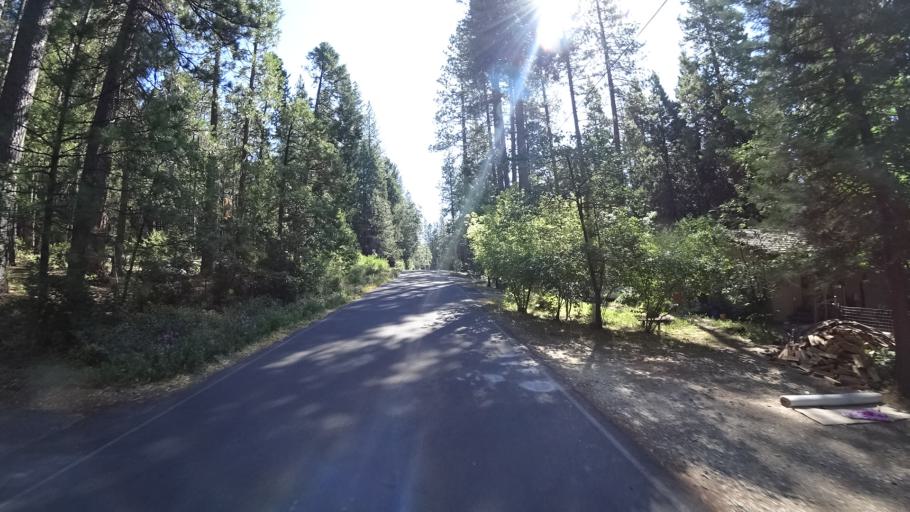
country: US
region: California
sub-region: Calaveras County
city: Arnold
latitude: 38.2383
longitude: -120.3700
